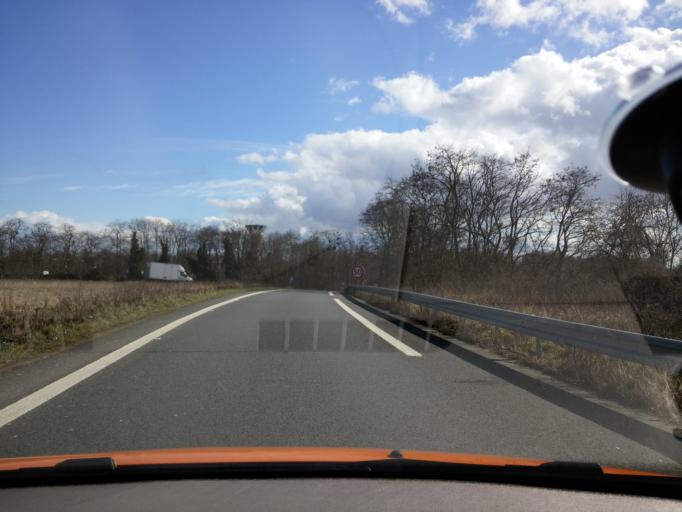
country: FR
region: Ile-de-France
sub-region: Departement de l'Essonne
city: Chilly-Mazarin
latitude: 48.7100
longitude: 2.3044
